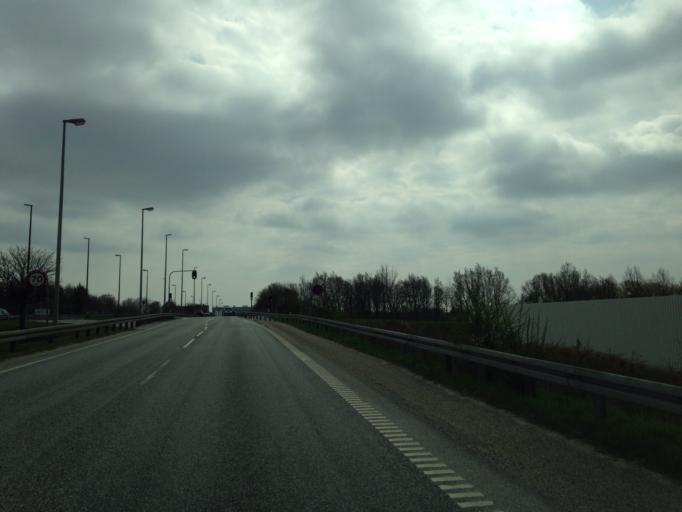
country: DK
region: Capital Region
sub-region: Ishoj Kommune
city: Ishoj
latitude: 55.6203
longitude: 12.3409
